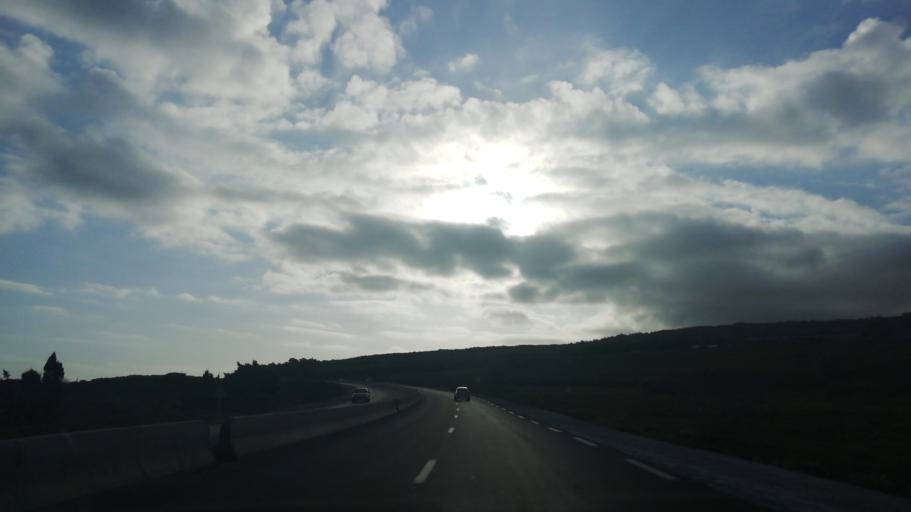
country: DZ
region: Mostaganem
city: Mostaganem
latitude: 36.1129
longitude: 0.2451
